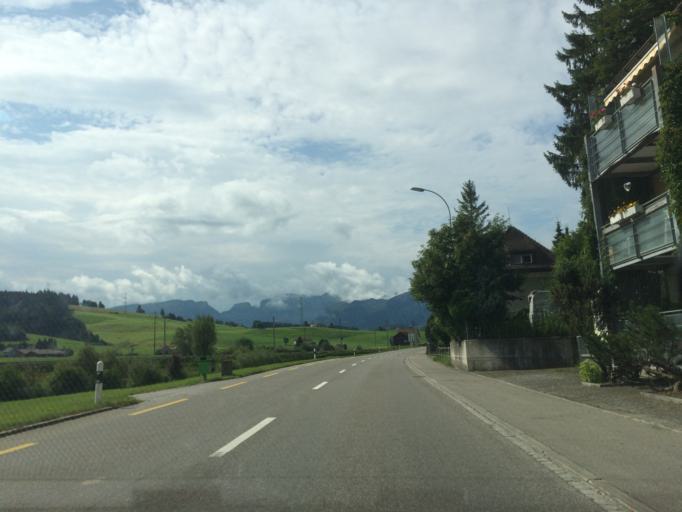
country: CH
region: Appenzell Ausserrhoden
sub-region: Bezirk Mittelland
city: Gais
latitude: 47.3579
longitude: 9.4438
